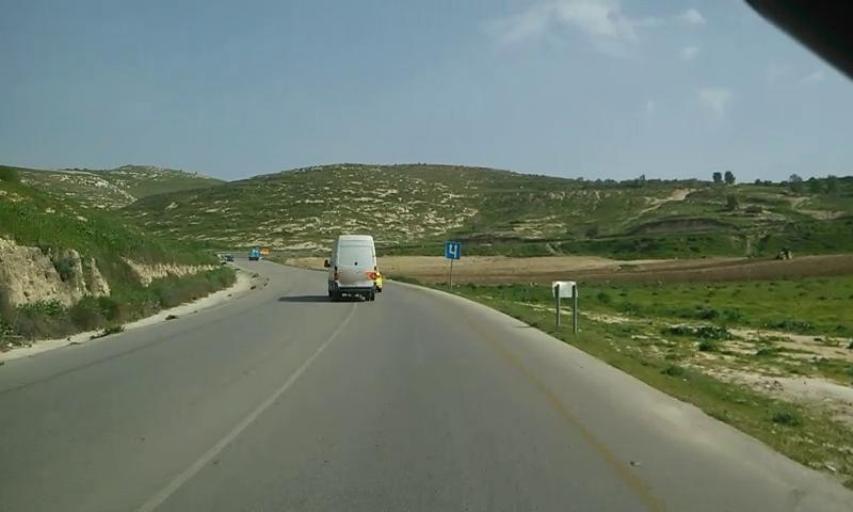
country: PS
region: West Bank
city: `Arrabah
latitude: 32.3842
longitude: 35.2148
